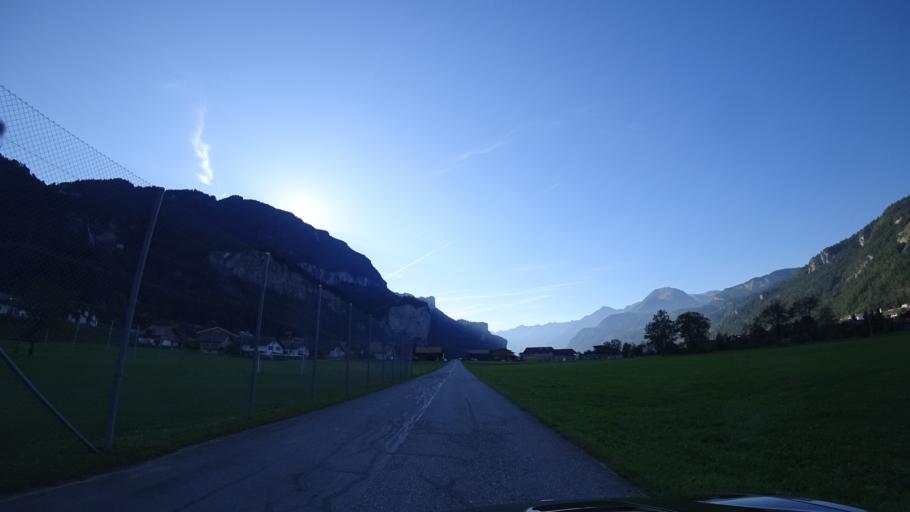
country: CH
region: Bern
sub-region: Interlaken-Oberhasli District
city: Meiringen
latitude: 46.7206
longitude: 8.1937
